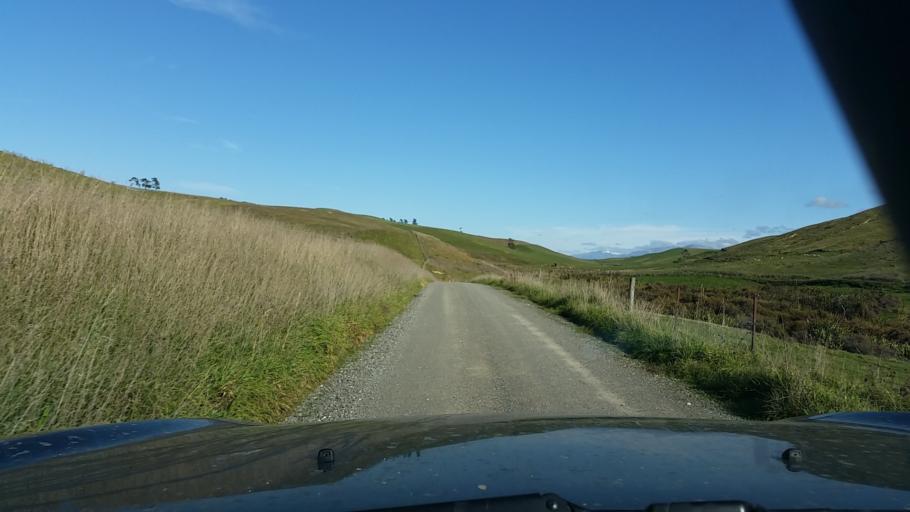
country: NZ
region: Marlborough
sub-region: Marlborough District
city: Blenheim
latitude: -41.6698
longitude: 174.1326
